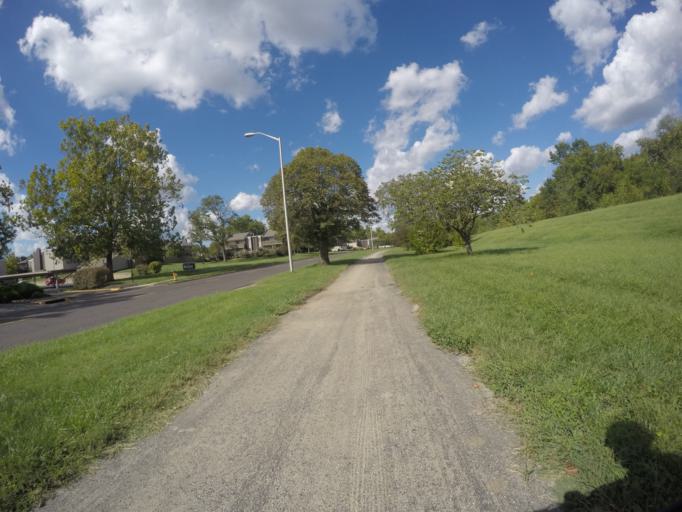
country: US
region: Kansas
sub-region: Johnson County
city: Overland Park
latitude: 38.9394
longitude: -94.6753
